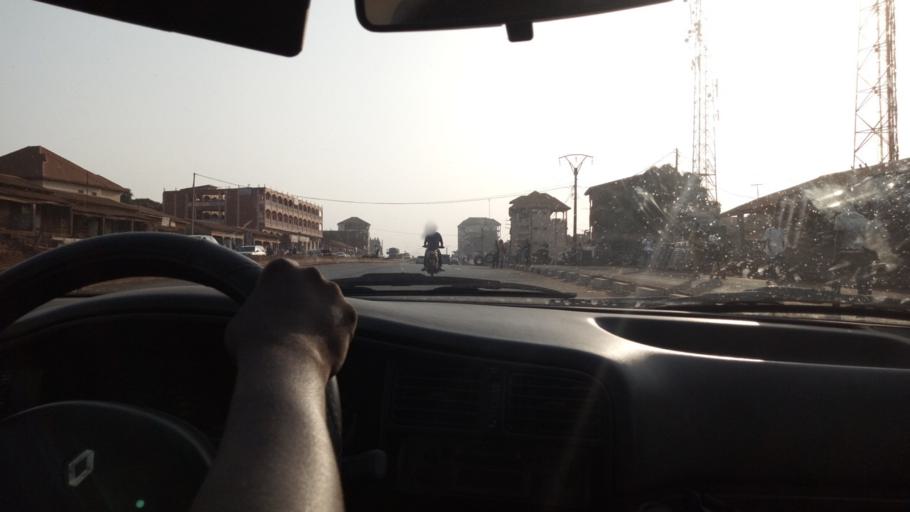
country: GN
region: Kindia
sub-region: Prefecture de Dubreka
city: Dubreka
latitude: 9.6797
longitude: -13.5378
